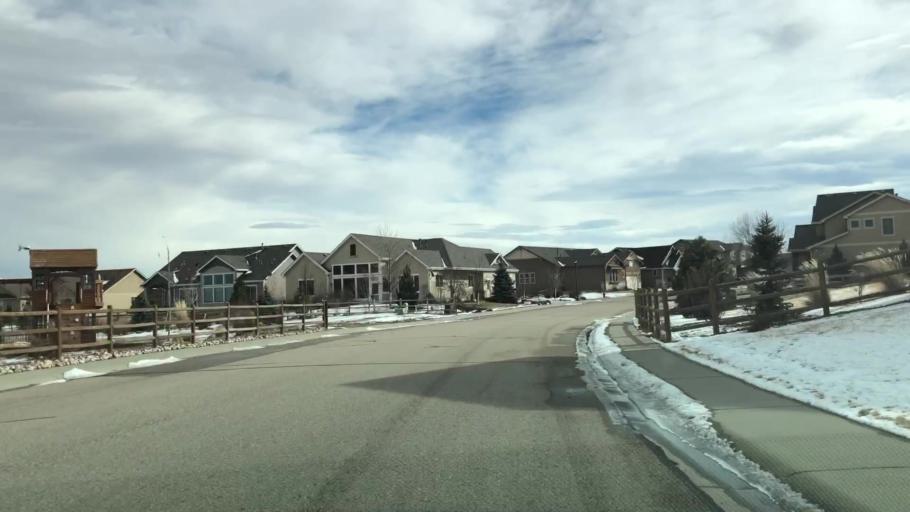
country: US
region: Colorado
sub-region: Weld County
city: Windsor
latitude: 40.4528
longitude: -104.9534
